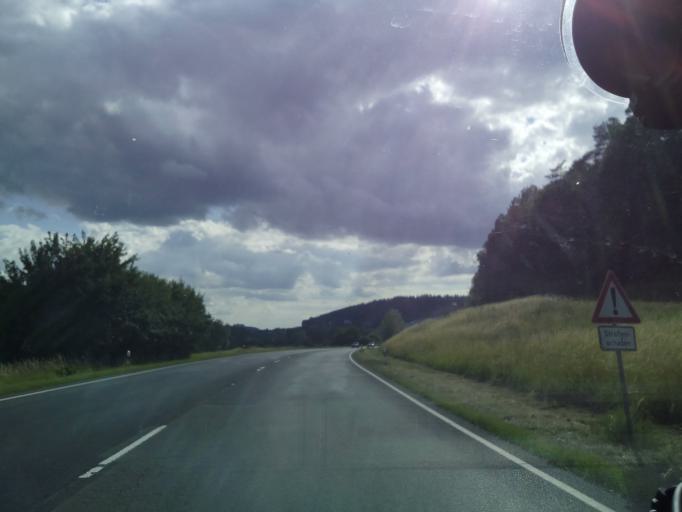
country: DE
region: Bavaria
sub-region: Upper Franconia
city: Rodental
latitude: 50.3098
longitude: 11.0747
